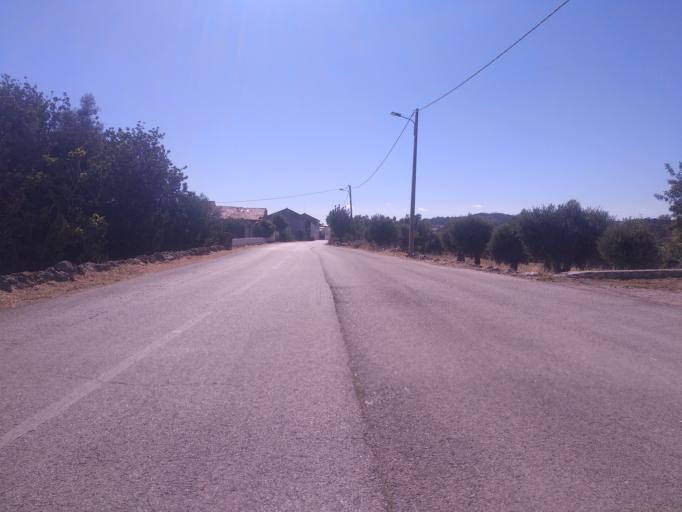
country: PT
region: Faro
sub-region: Sao Bras de Alportel
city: Sao Bras de Alportel
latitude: 37.1701
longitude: -7.8918
